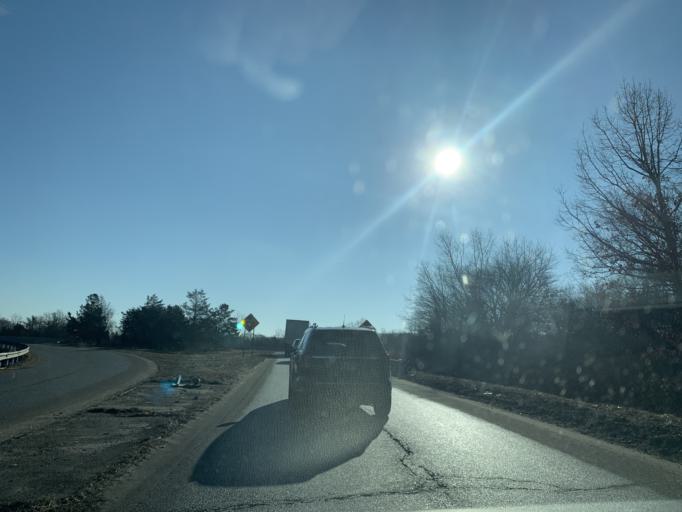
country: US
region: Massachusetts
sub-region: Essex County
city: Methuen
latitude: 42.7271
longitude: -71.2076
